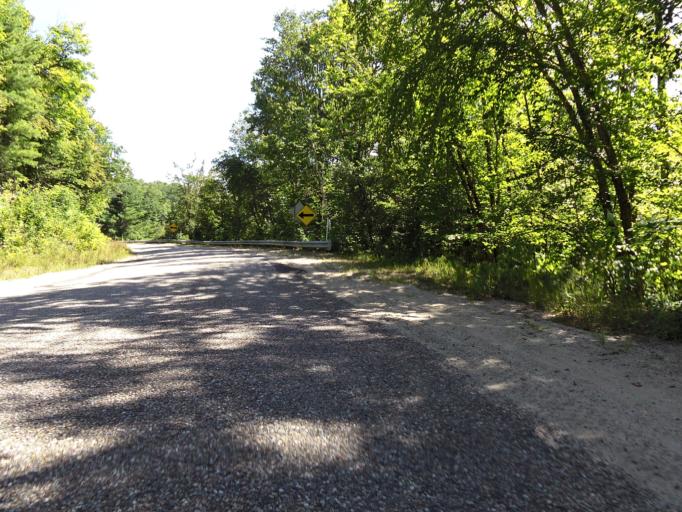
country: CA
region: Quebec
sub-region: Outaouais
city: Maniwaki
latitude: 46.2174
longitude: -76.0810
